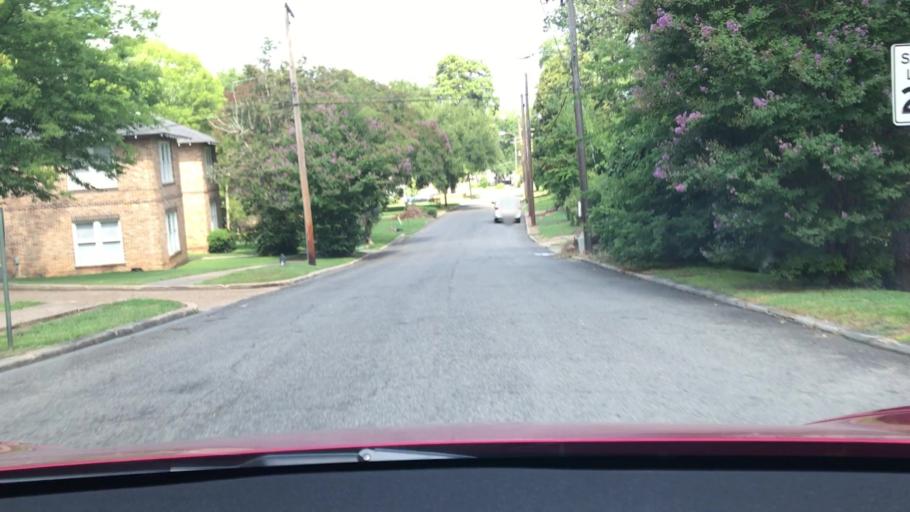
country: US
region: Louisiana
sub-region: Bossier Parish
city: Bossier City
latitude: 32.4807
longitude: -93.7336
